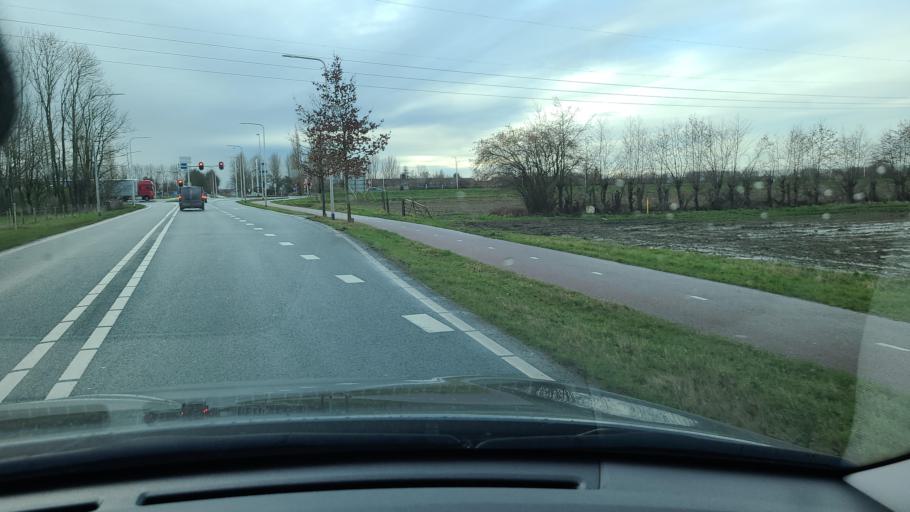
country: NL
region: Gelderland
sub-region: Gemeente Druten
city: Druten
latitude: 51.8740
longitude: 5.5323
